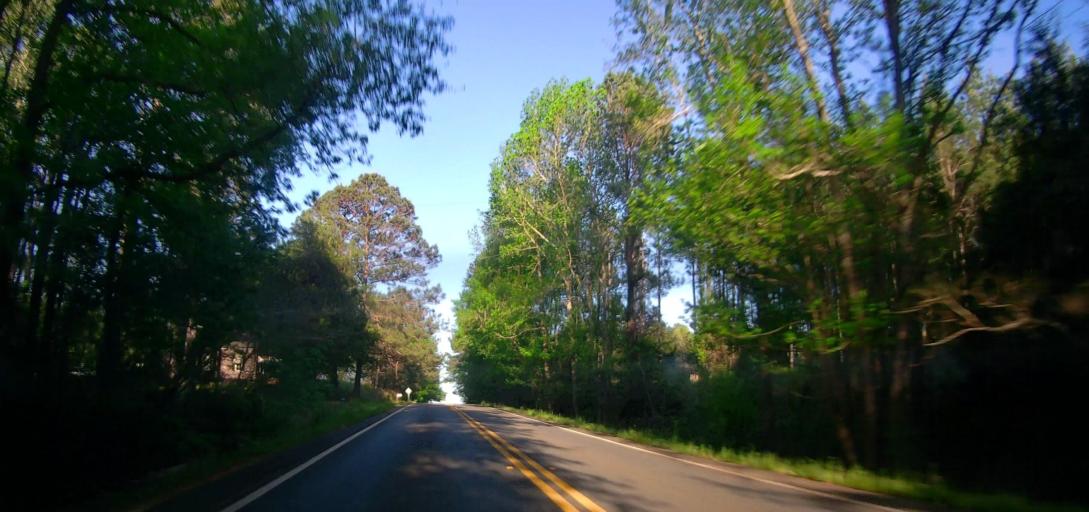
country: US
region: Georgia
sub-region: Schley County
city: Ellaville
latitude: 32.3222
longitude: -84.2374
